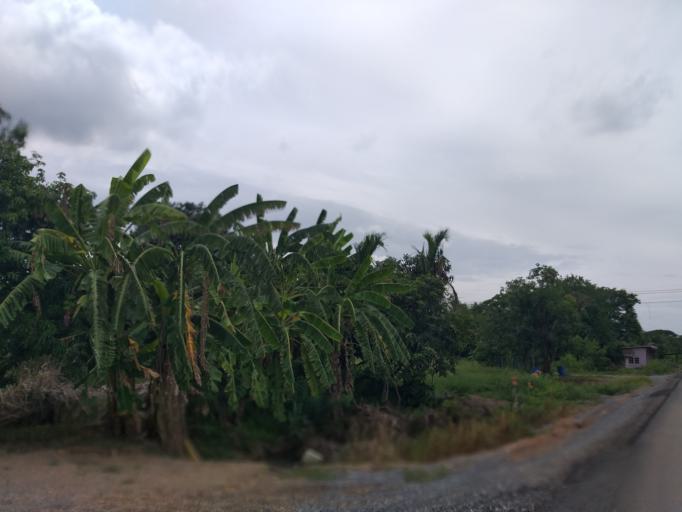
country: TH
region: Pathum Thani
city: Nong Suea
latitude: 14.0393
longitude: 100.8700
